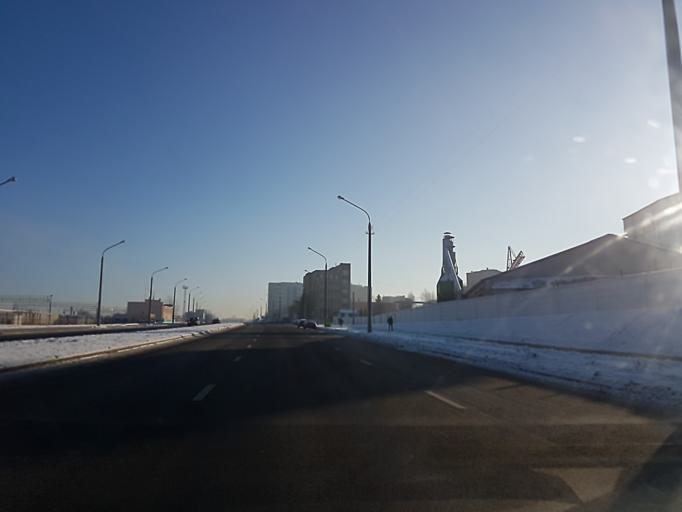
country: BY
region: Minsk
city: Minsk
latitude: 53.9028
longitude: 27.5261
